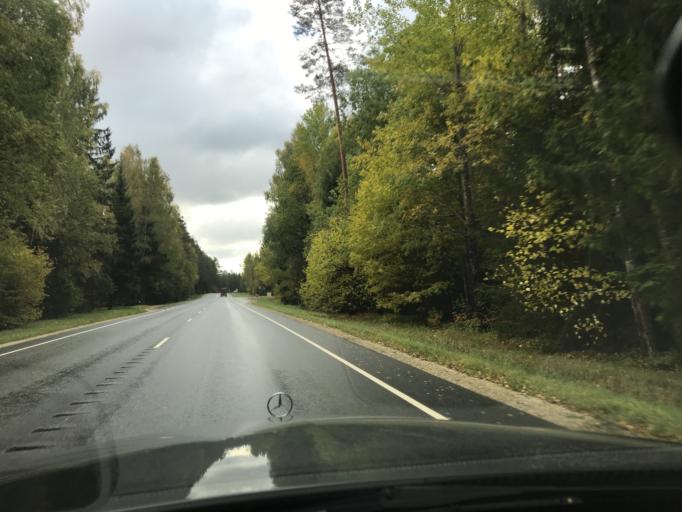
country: EE
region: Viljandimaa
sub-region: Karksi vald
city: Karksi-Nuia
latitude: 58.0311
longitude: 25.6502
